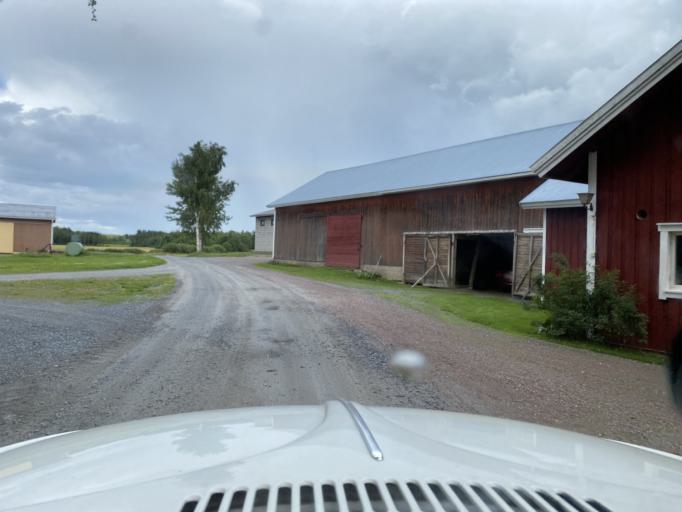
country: FI
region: Pirkanmaa
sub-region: Lounais-Pirkanmaa
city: Punkalaidun
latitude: 61.1221
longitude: 23.0586
